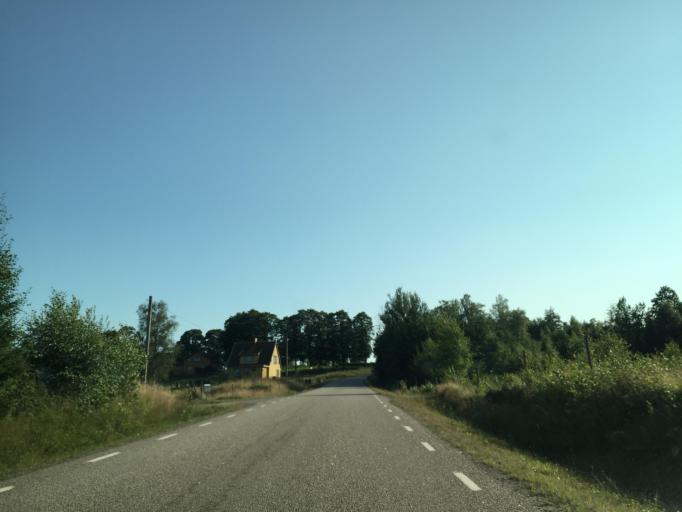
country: SE
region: Vaestra Goetaland
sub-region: Lilla Edets Kommun
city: Lilla Edet
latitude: 58.1676
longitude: 12.0765
